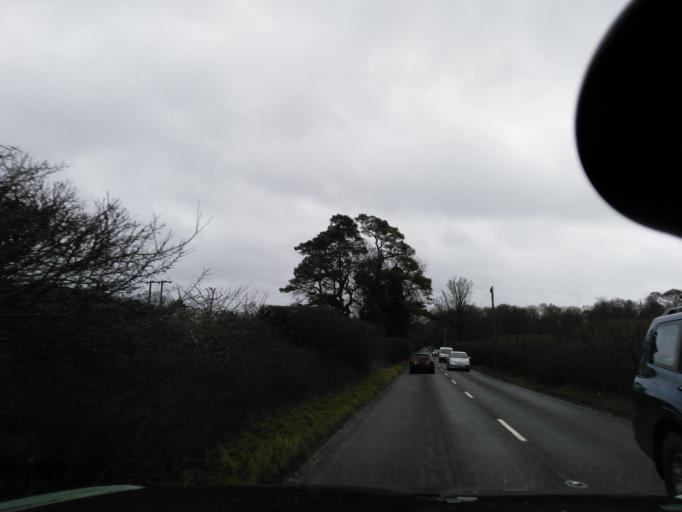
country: GB
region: England
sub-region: Wiltshire
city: Neston
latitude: 51.4013
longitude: -2.2164
